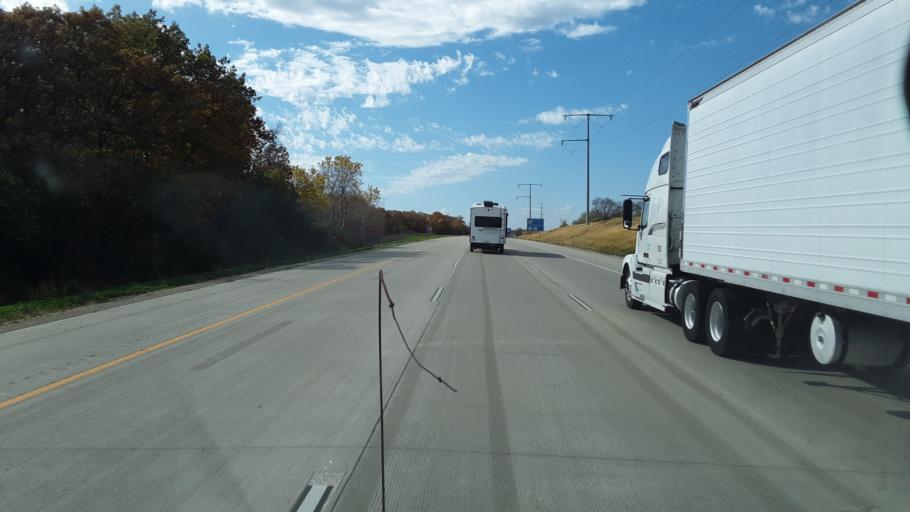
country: US
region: Wisconsin
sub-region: Dane County
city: Cottage Grove
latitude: 42.9993
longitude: -89.1792
